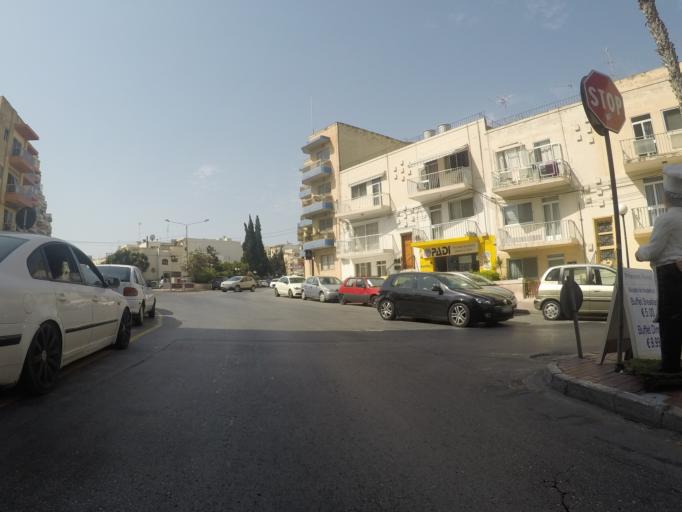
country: MT
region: Saint Paul's Bay
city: San Pawl il-Bahar
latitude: 35.9507
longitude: 14.4145
